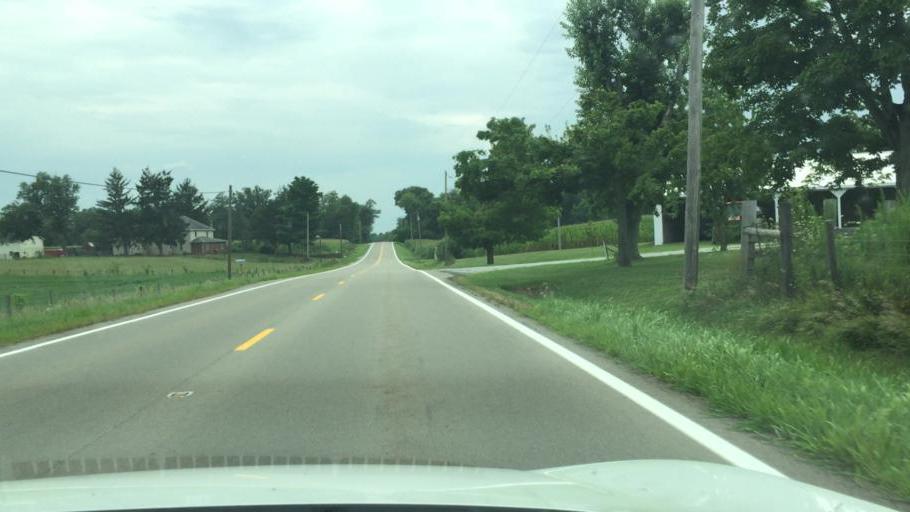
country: US
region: Ohio
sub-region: Clark County
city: Northridge
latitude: 40.0152
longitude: -83.6855
